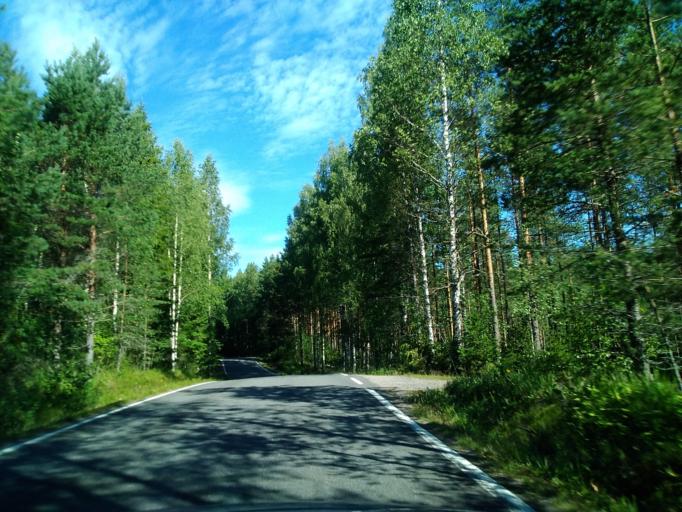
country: FI
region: Uusimaa
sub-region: Helsinki
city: Kaerkoelae
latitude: 60.7743
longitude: 24.0736
